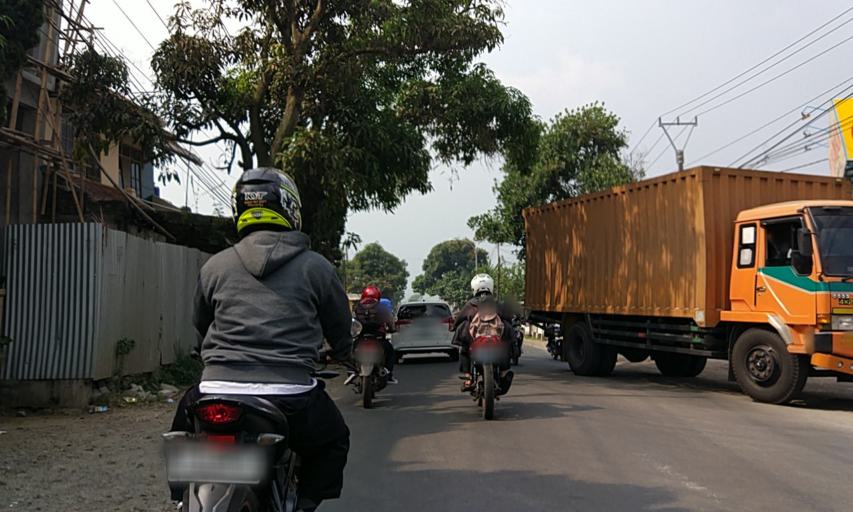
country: ID
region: West Java
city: Banjaran
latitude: -7.0513
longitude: 107.5766
